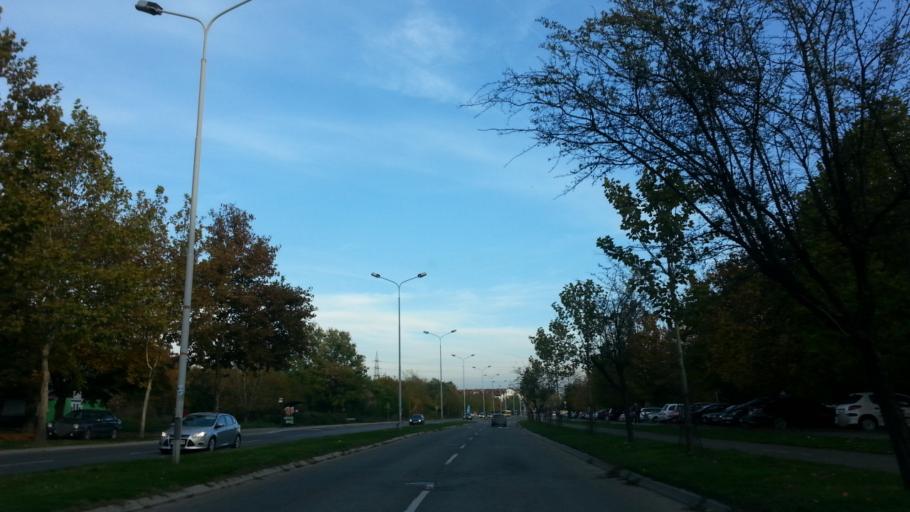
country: RS
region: Central Serbia
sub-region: Belgrade
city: Zemun
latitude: 44.8200
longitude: 20.3802
